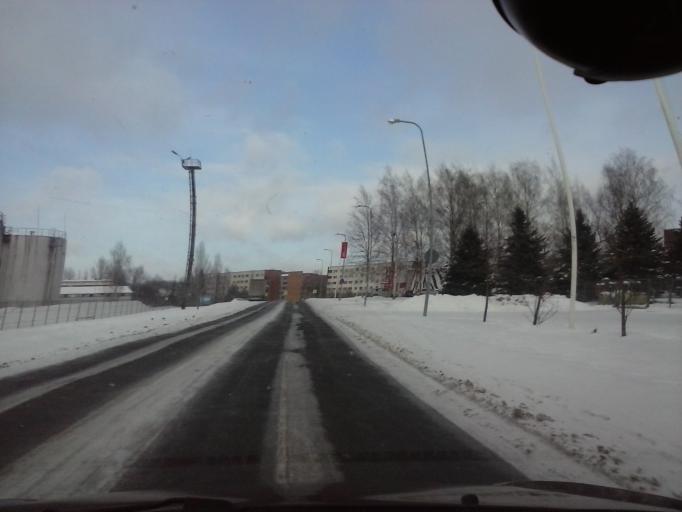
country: EE
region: Viljandimaa
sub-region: Viljandi linn
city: Viljandi
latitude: 58.3548
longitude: 25.5764
